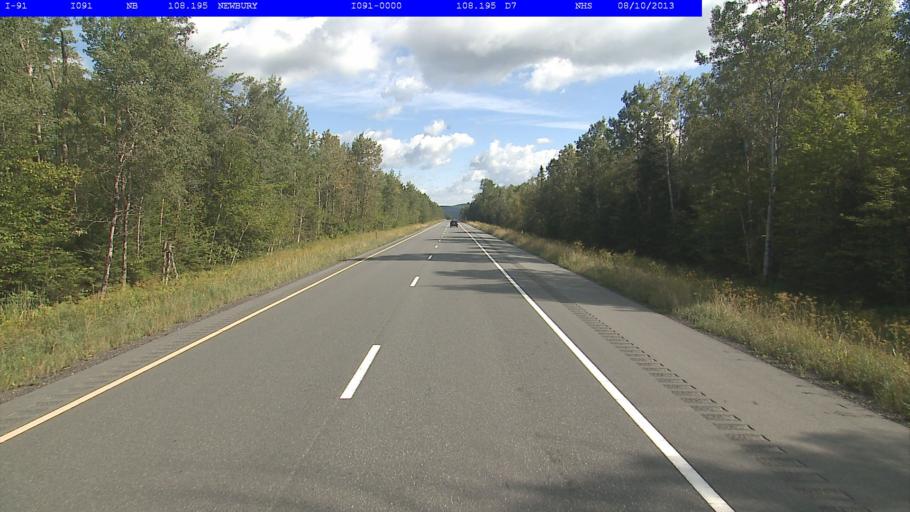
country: US
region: New Hampshire
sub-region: Grafton County
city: Woodsville
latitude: 44.1312
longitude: -72.1029
